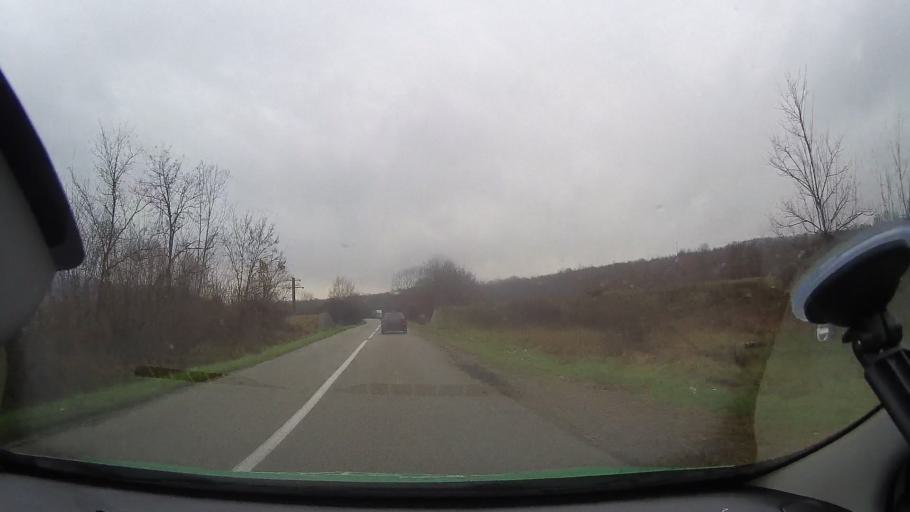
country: RO
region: Arad
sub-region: Comuna Ignesti
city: Ignesti
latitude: 46.3838
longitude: 22.1604
